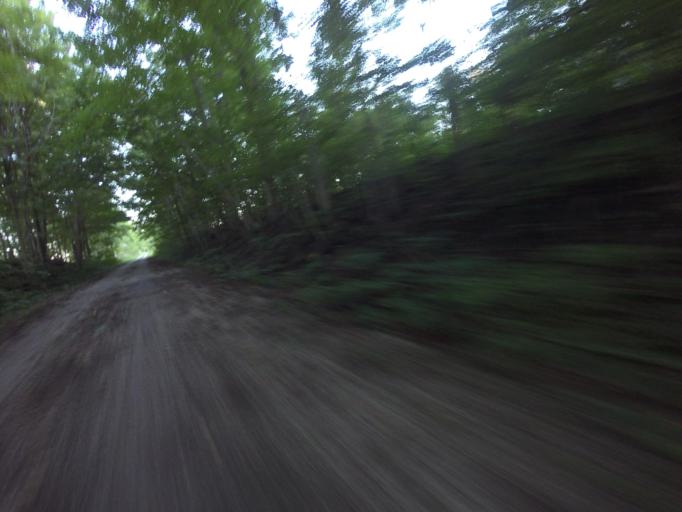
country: CA
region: Ontario
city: Goderich
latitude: 43.7513
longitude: -81.6616
